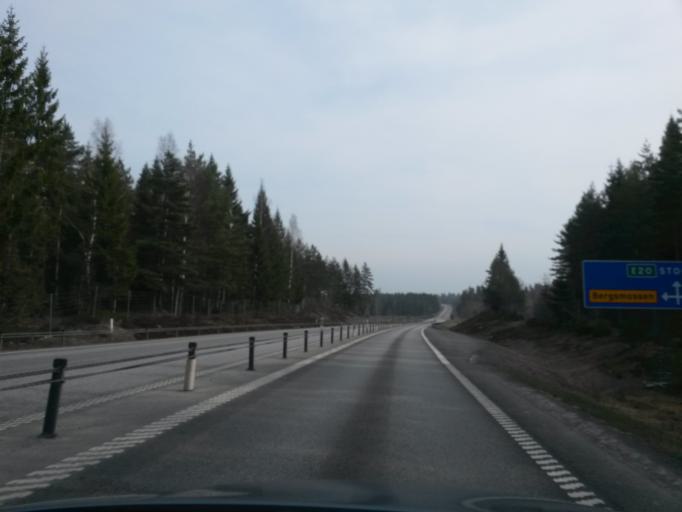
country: SE
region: OErebro
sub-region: Laxa Kommun
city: Laxa
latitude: 58.9566
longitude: 14.5125
